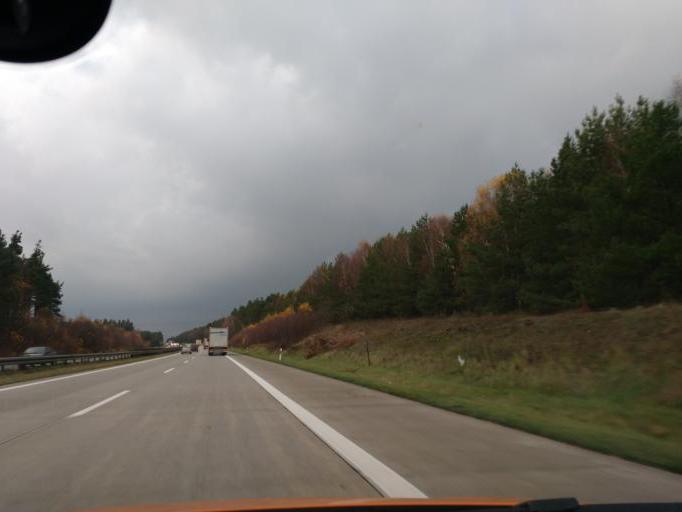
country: DE
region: Brandenburg
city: Heiligengrabe
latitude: 53.1599
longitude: 12.3899
